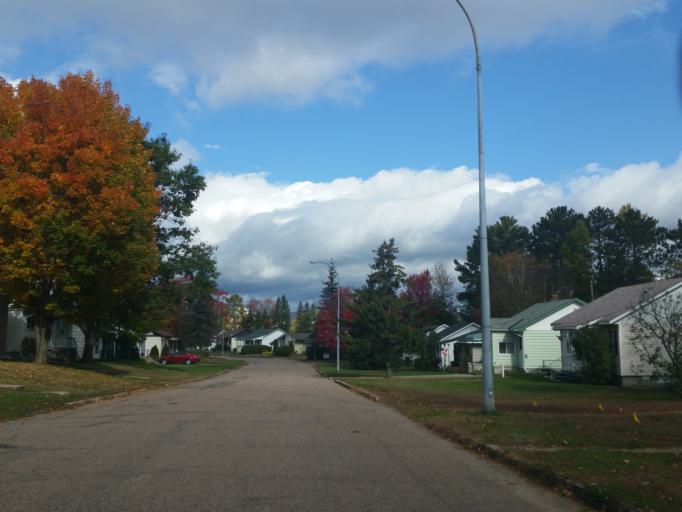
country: CA
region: Ontario
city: Deep River
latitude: 46.0981
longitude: -77.4884
